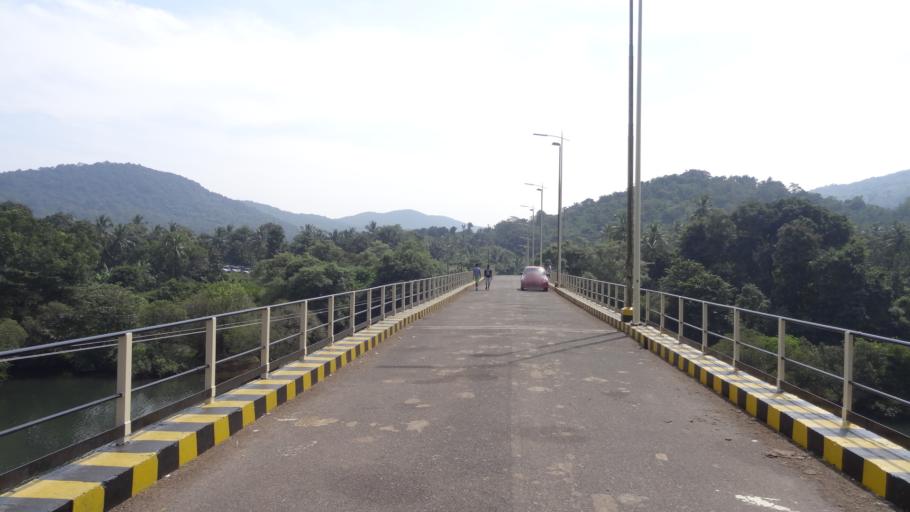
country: IN
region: Goa
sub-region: North Goa
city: Palle
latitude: 15.4674
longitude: 74.0830
